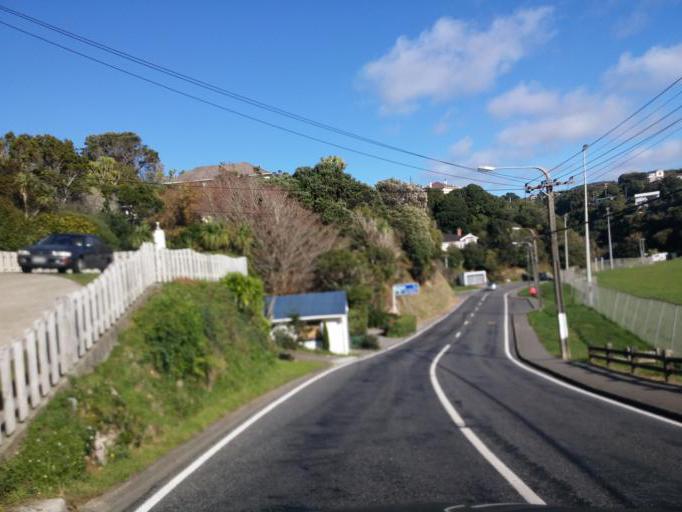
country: NZ
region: Wellington
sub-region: Wellington City
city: Kelburn
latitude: -41.2785
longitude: 174.7556
